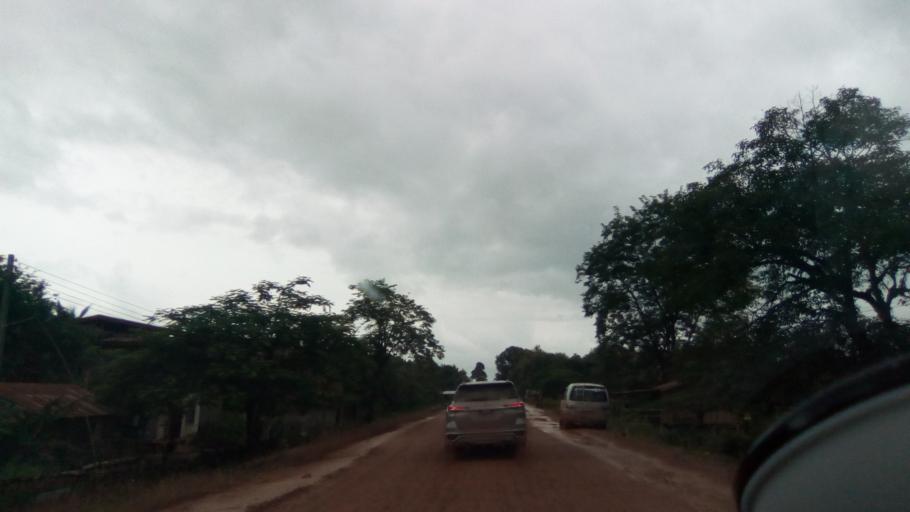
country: LA
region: Attapu
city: Attapu
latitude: 14.7463
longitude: 106.6972
